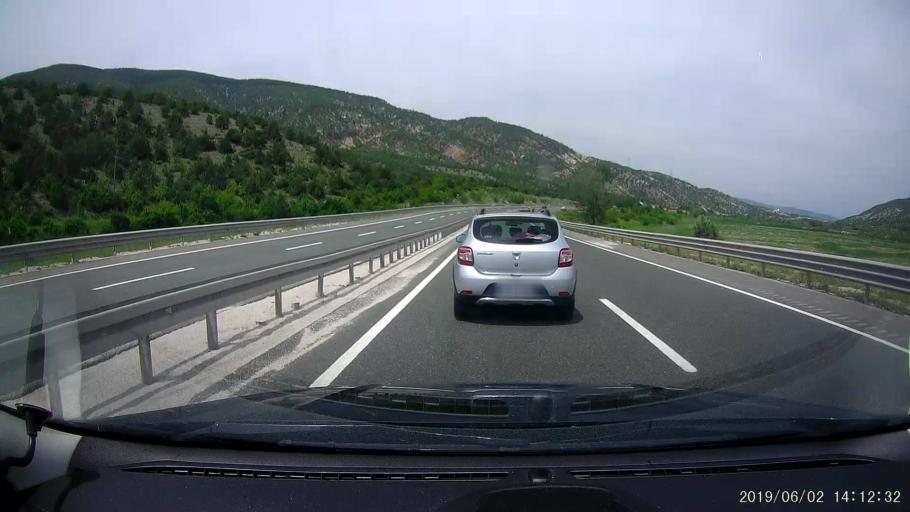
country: TR
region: Cankiri
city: Yaprakli
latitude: 40.9148
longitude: 33.8114
